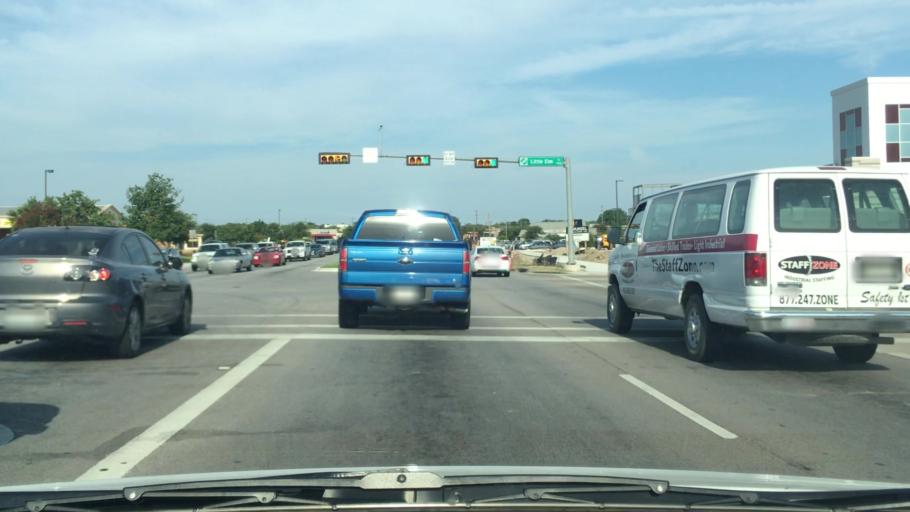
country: US
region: Texas
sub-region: Williamson County
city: Cedar Park
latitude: 30.4812
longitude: -97.8279
